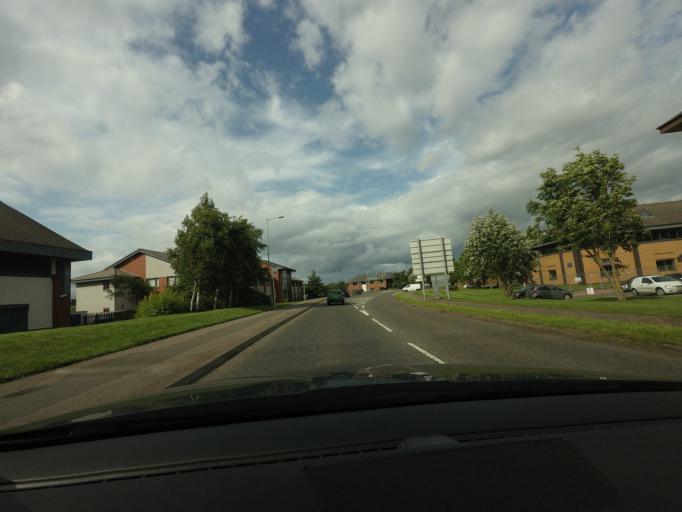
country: GB
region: Scotland
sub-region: Highland
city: Inverness
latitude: 57.4726
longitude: -4.1898
